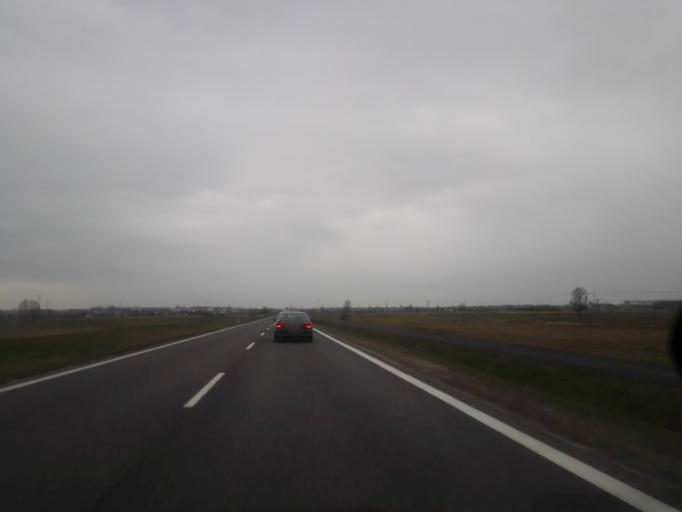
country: PL
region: Podlasie
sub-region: Powiat grajewski
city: Grajewo
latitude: 53.6559
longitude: 22.4951
